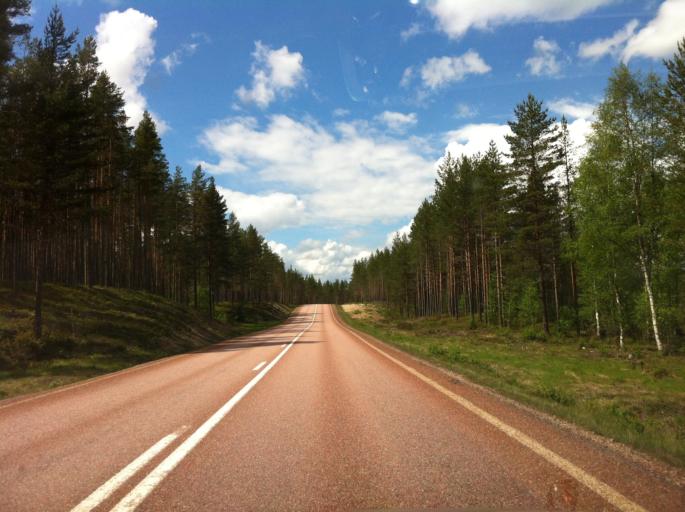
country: SE
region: Dalarna
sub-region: Malung-Saelens kommun
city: Malung
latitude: 60.7573
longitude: 13.5140
